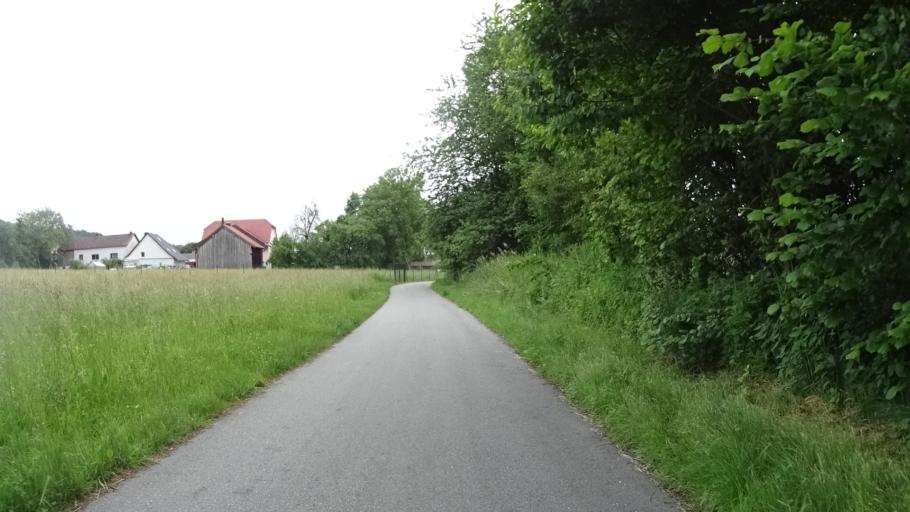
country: DE
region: Bavaria
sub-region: Lower Bavaria
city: Vilshofen
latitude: 48.6222
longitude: 13.2245
